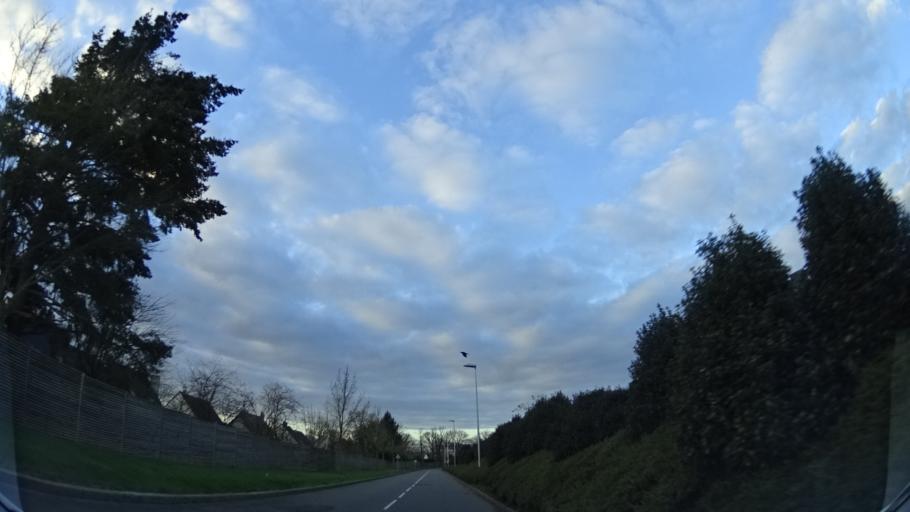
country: FR
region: Brittany
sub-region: Departement d'Ille-et-Vilaine
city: Betton
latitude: 48.1825
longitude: -1.6557
